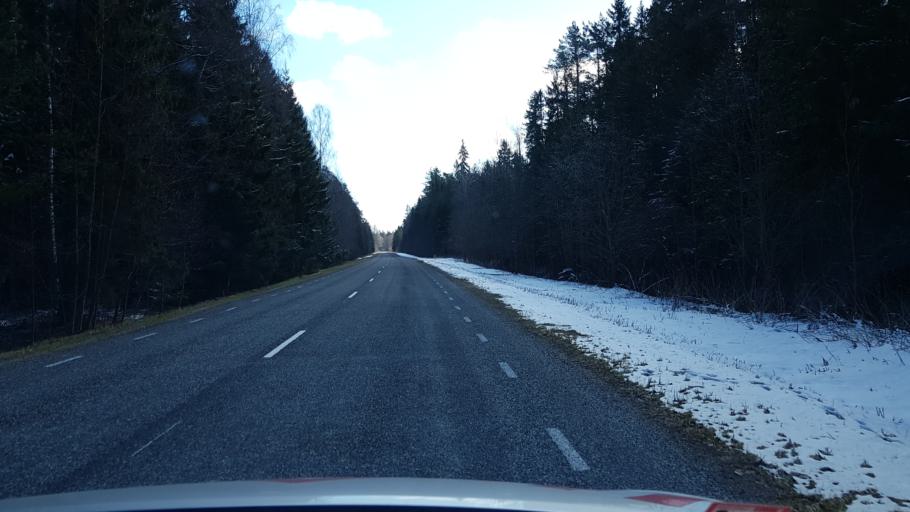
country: EE
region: Harju
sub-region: Loksa linn
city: Loksa
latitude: 59.5653
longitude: 25.9467
